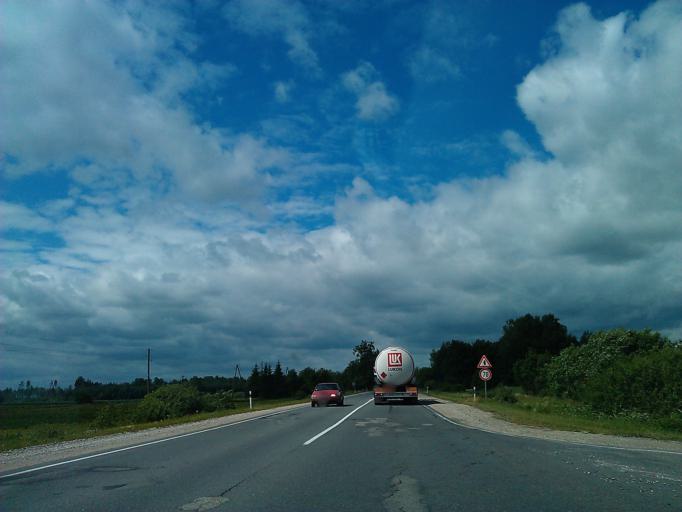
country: LV
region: Engure
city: Smarde
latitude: 56.9130
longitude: 23.3638
